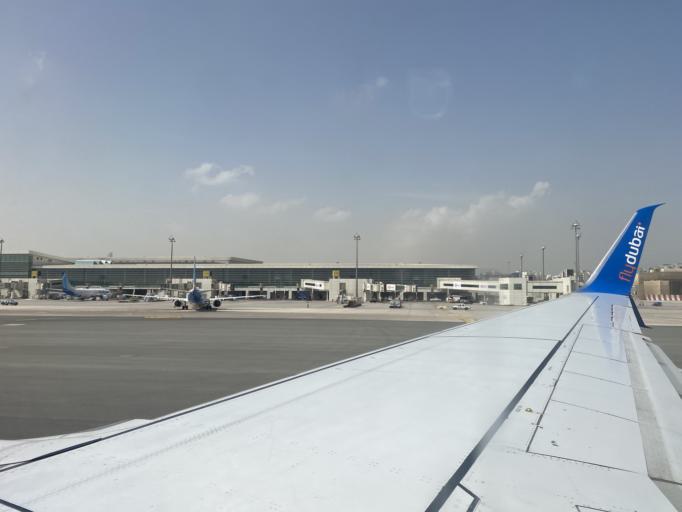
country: AE
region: Ash Shariqah
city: Sharjah
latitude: 25.2619
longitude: 55.3431
